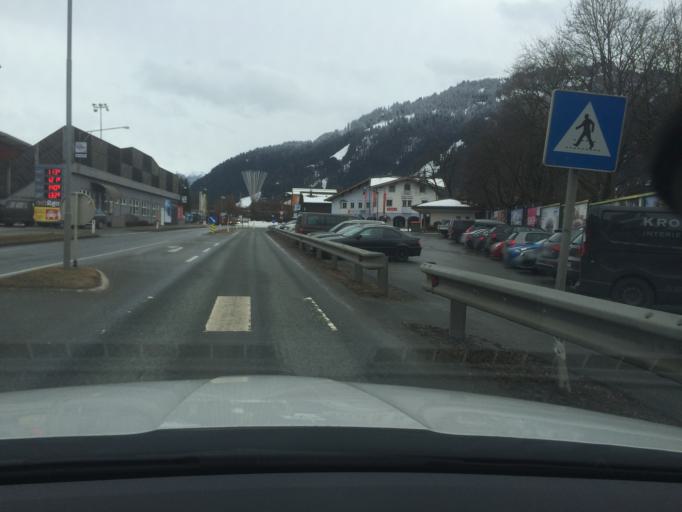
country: AT
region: Tyrol
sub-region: Politischer Bezirk Kitzbuhel
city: Kitzbuhel
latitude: 47.4448
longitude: 12.3984
